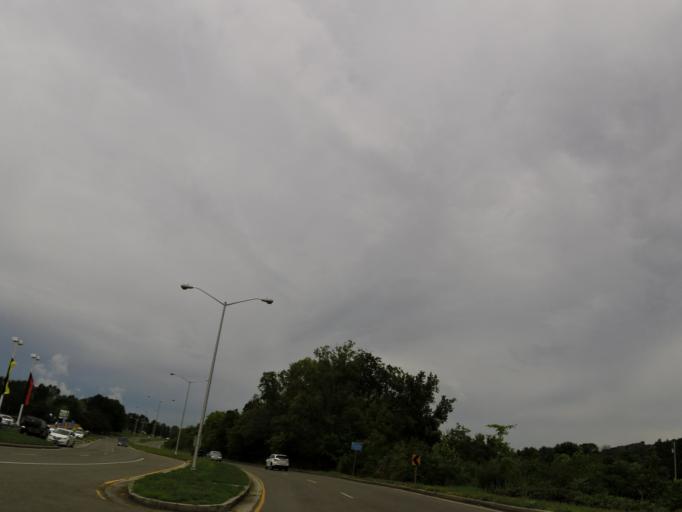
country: US
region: Tennessee
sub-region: Knox County
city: Farragut
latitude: 35.9014
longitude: -84.1377
